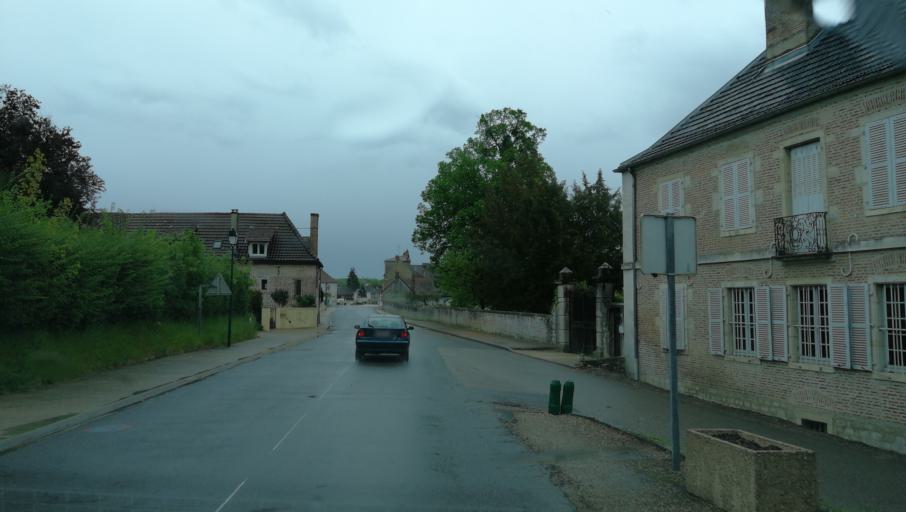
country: FR
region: Bourgogne
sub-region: Departement de Saone-et-Loire
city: Pierre-de-Bresse
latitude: 46.8866
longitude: 5.2587
